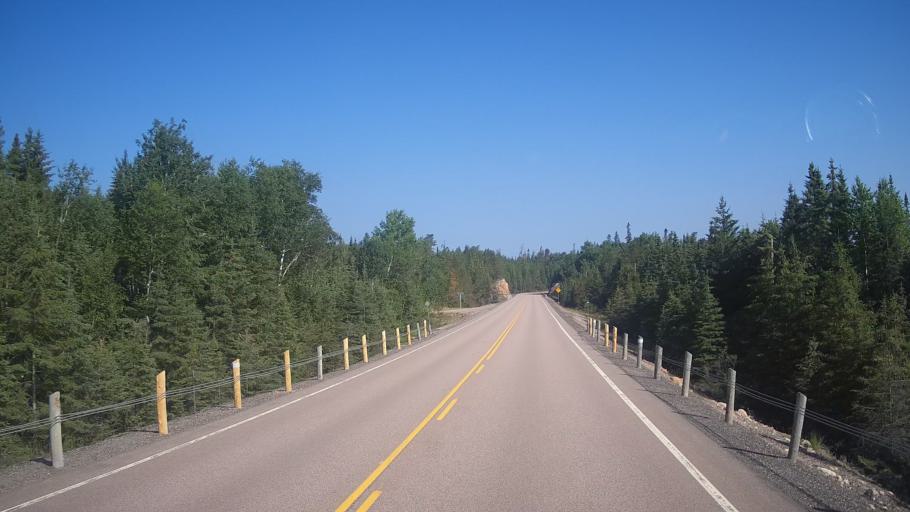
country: CA
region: Ontario
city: Rayside-Balfour
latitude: 46.9784
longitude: -81.6313
